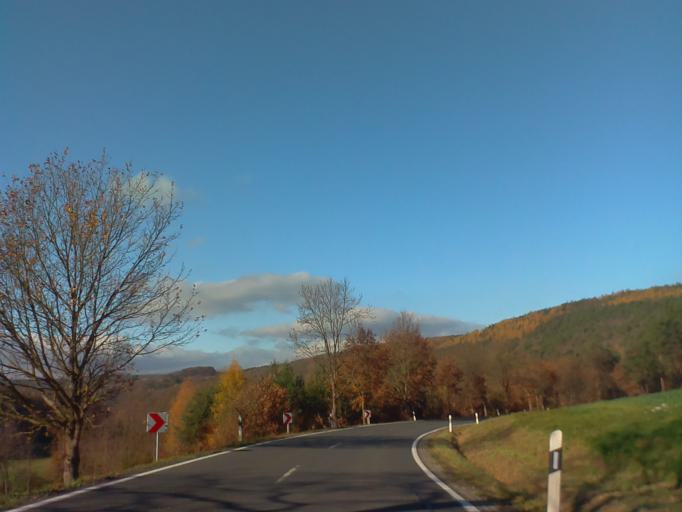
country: DE
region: Bavaria
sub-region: Regierungsbezirk Unterfranken
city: Niederlauer
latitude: 50.2913
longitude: 10.1537
